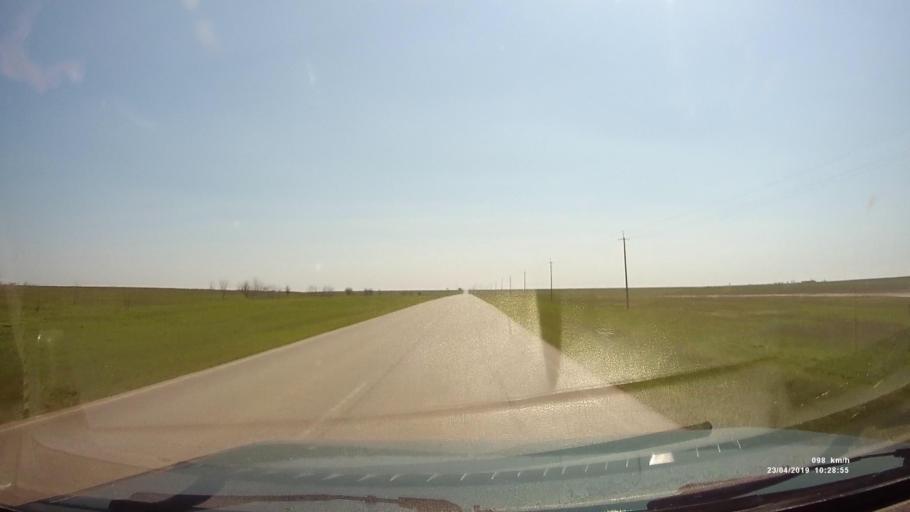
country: RU
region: Kalmykiya
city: Yashalta
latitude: 46.6020
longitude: 42.5166
